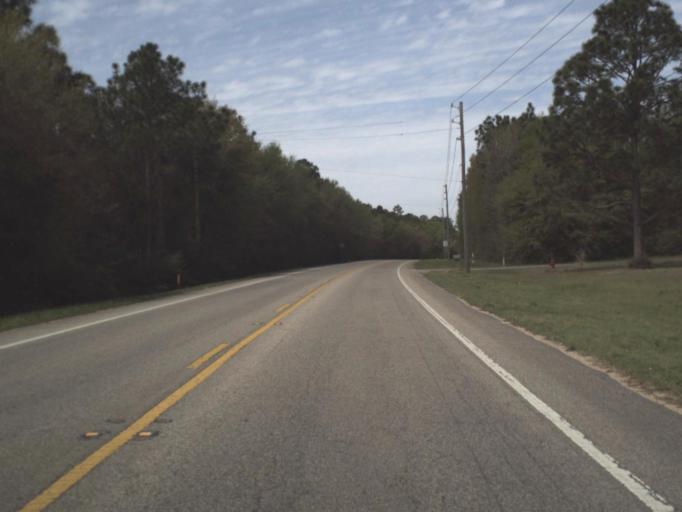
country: US
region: Florida
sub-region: Okaloosa County
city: Crestview
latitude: 30.7500
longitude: -86.4747
